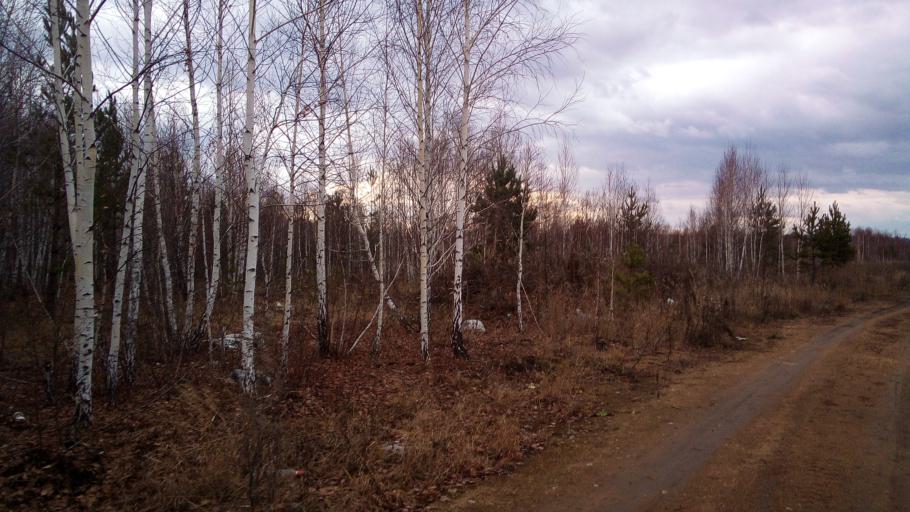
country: RU
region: Chelyabinsk
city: Sargazy
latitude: 55.1251
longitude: 61.2487
